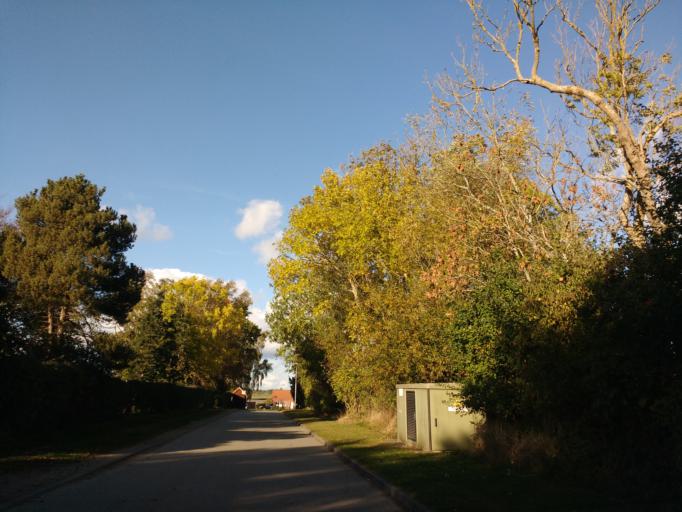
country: DE
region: Schleswig-Holstein
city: Grossenbrode
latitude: 54.4271
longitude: 11.1090
